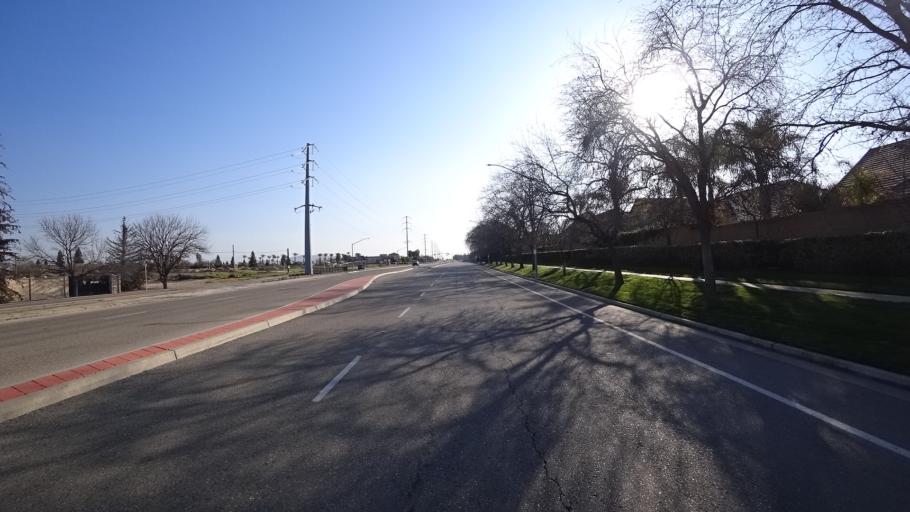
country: US
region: California
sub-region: Fresno County
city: Clovis
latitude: 36.8955
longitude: -119.7509
